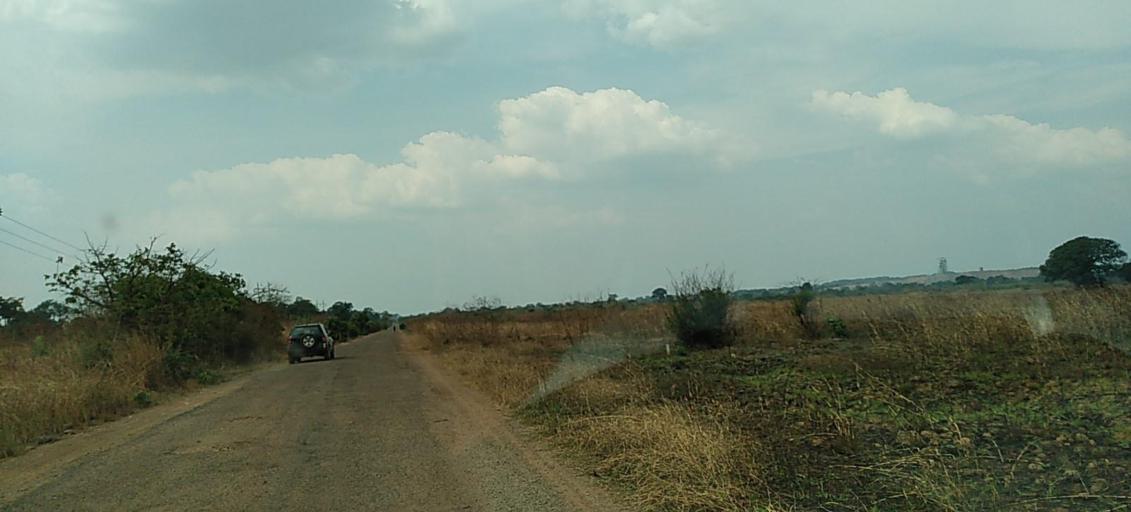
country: ZM
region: Copperbelt
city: Chililabombwe
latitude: -12.3926
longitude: 27.8063
